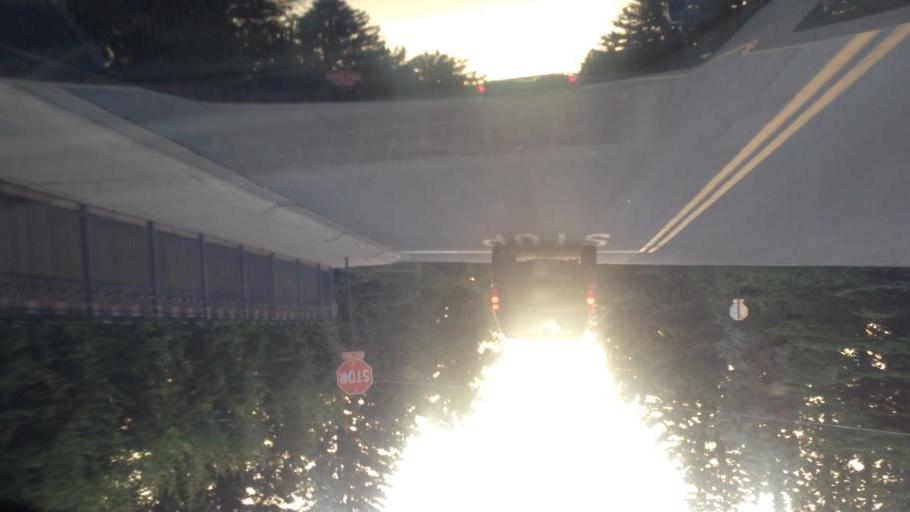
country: US
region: Nevada
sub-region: Washoe County
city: Reno
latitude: 39.4919
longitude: -119.8278
